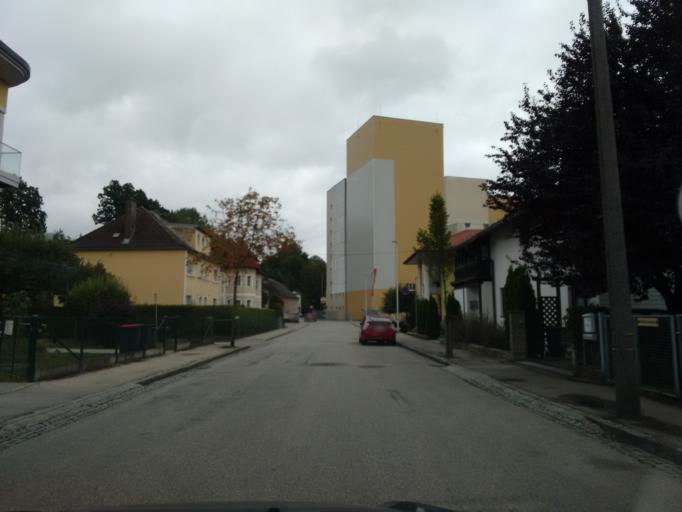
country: AT
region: Upper Austria
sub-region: Politischer Bezirk Grieskirchen
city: Grieskirchen
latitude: 48.2366
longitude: 13.8223
